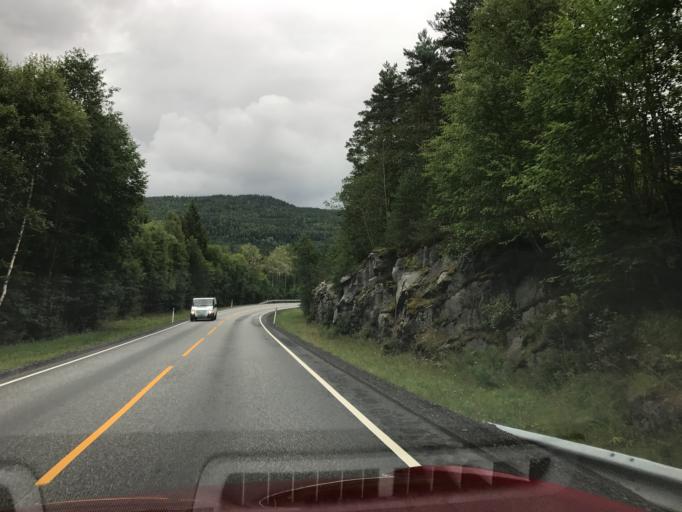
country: NO
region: Buskerud
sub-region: Rollag
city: Rollag
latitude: 60.0378
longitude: 9.2153
